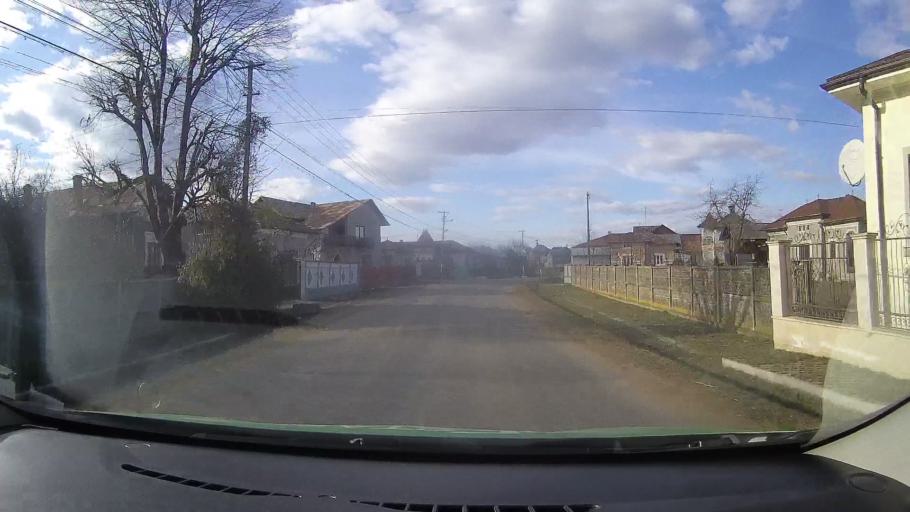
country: RO
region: Dambovita
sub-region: Comuna Ulmi
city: Ulmi
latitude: 44.8787
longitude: 25.5168
